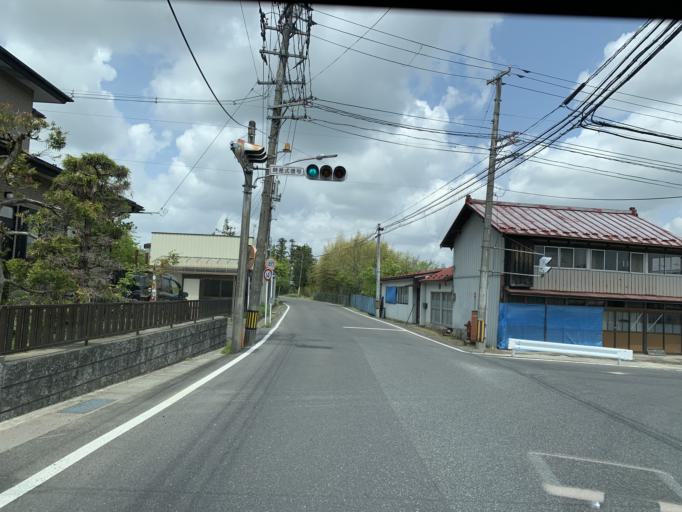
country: JP
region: Miyagi
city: Kogota
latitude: 38.6645
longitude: 141.0654
